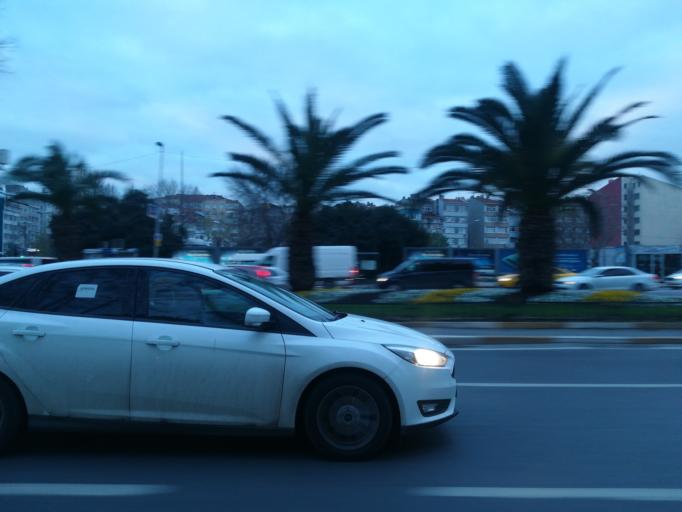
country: TR
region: Istanbul
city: Istanbul
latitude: 41.0166
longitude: 28.9410
